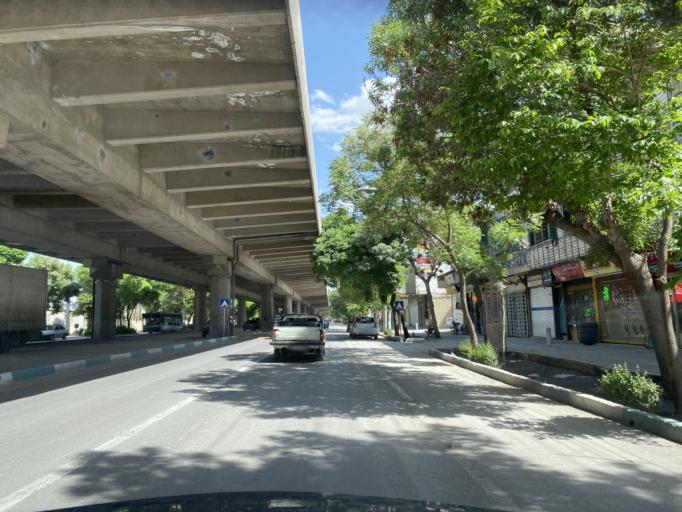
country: IR
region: Isfahan
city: Rehnan
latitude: 32.6902
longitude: 51.6301
